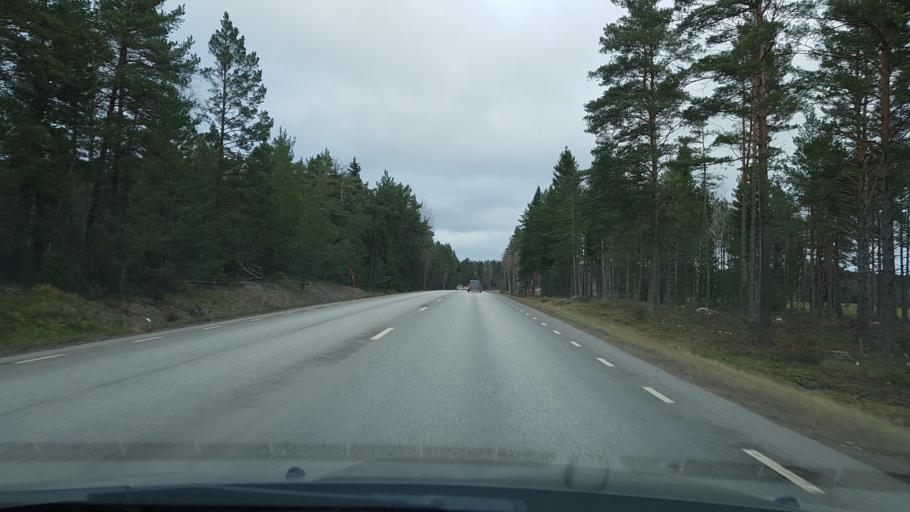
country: SE
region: Stockholm
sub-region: Norrtalje Kommun
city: Hallstavik
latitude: 60.0437
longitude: 18.5606
